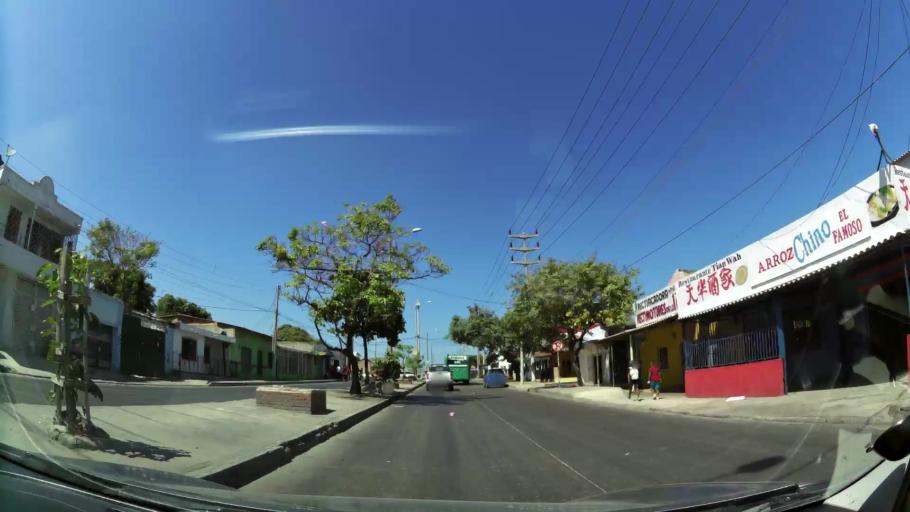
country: CO
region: Atlantico
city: Barranquilla
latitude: 10.9601
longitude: -74.7748
